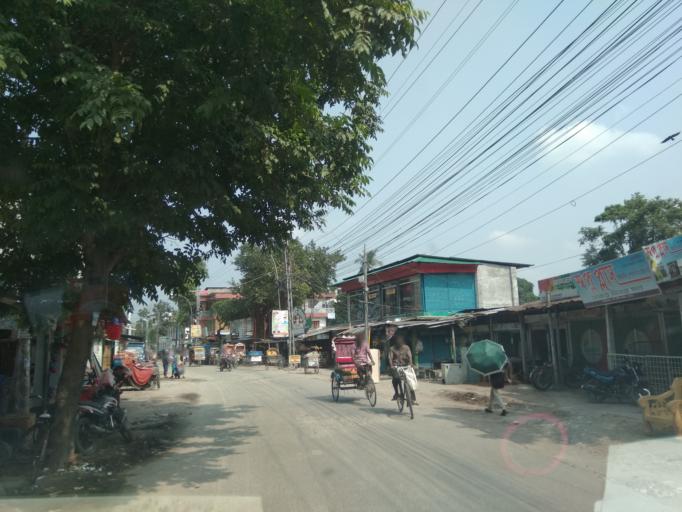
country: BD
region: Rangpur Division
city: Rangpur
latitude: 25.7592
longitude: 89.2330
